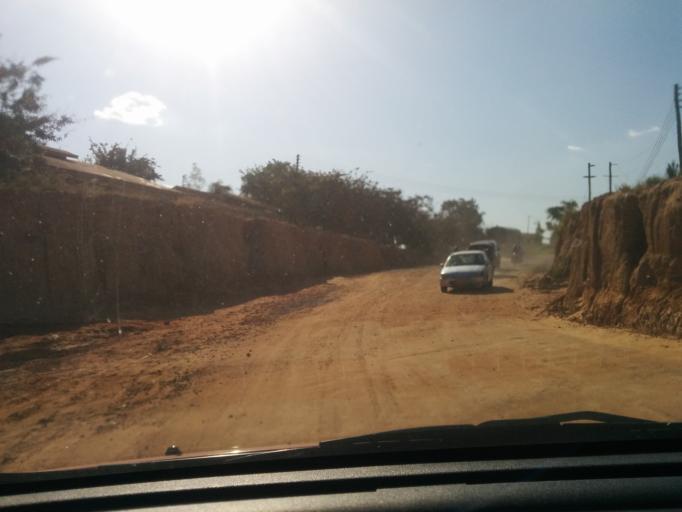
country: TZ
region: Dar es Salaam
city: Magomeni
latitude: -6.7657
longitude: 39.1222
